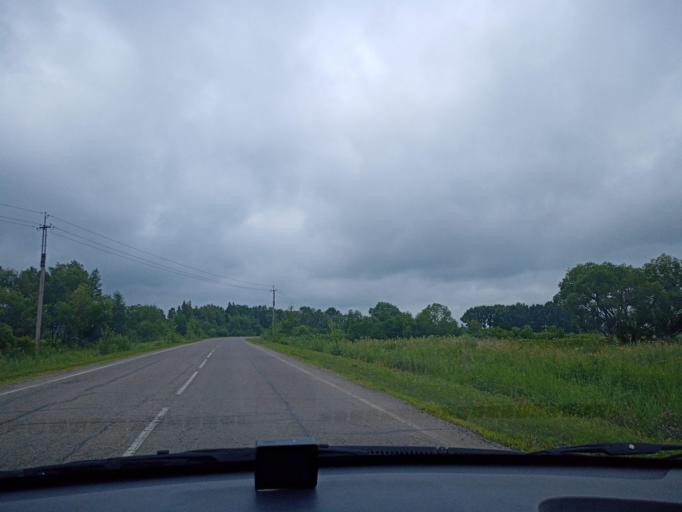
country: RU
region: Primorskiy
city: Novopokrovka
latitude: 45.8895
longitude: 134.8482
